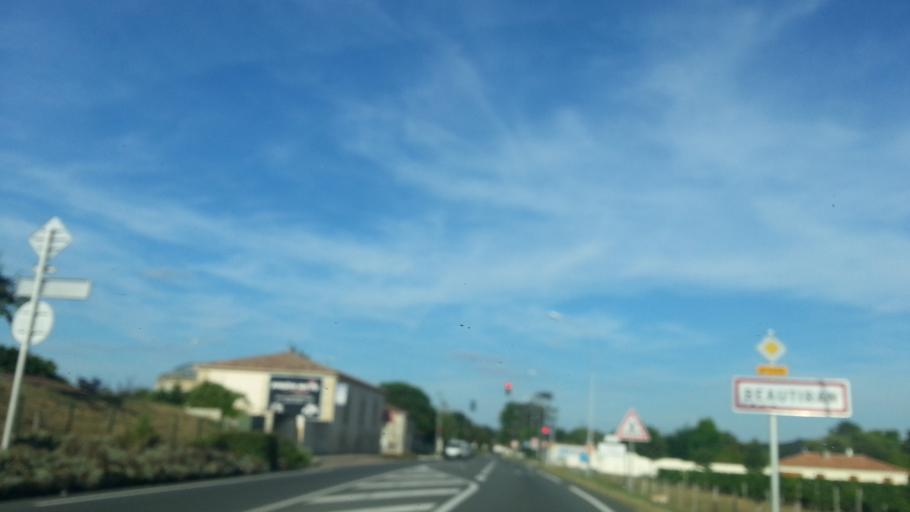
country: FR
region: Aquitaine
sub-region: Departement de la Gironde
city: Beautiran
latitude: 44.6992
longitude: -0.4624
